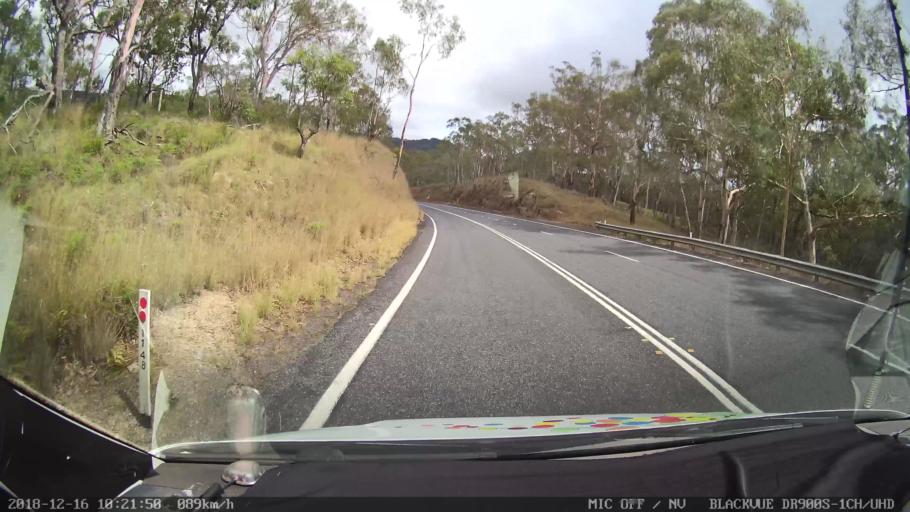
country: AU
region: New South Wales
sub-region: Tenterfield Municipality
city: Carrolls Creek
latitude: -29.2019
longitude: 152.0139
